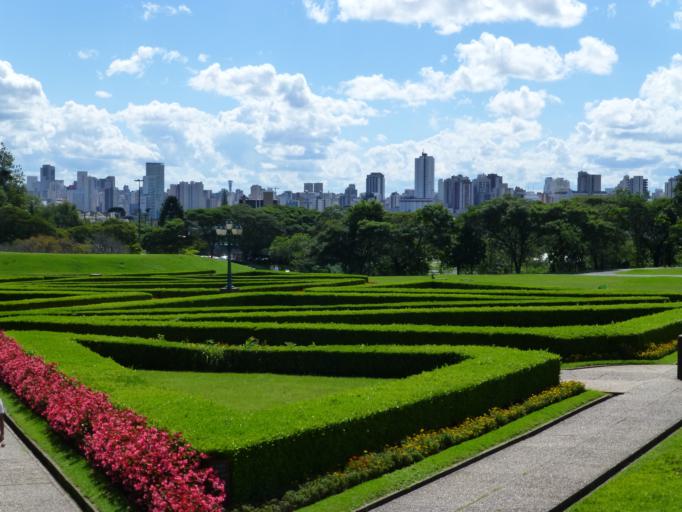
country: BR
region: Parana
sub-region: Curitiba
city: Curitiba
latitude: -25.4430
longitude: -49.2384
